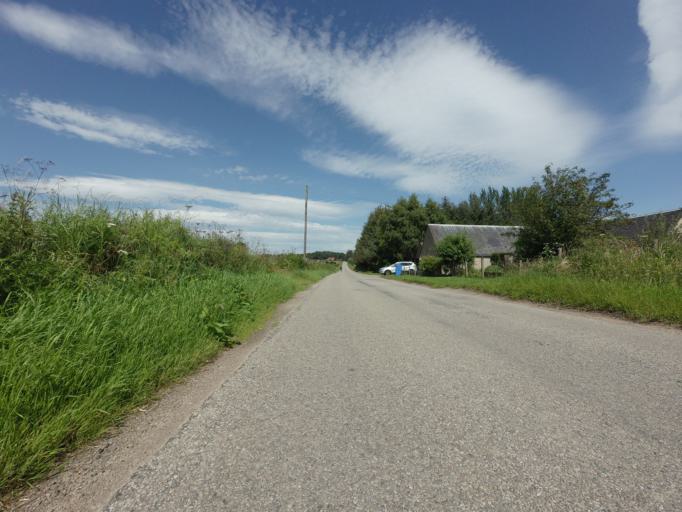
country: GB
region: Scotland
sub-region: Highland
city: Inverness
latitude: 57.5273
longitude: -4.3185
